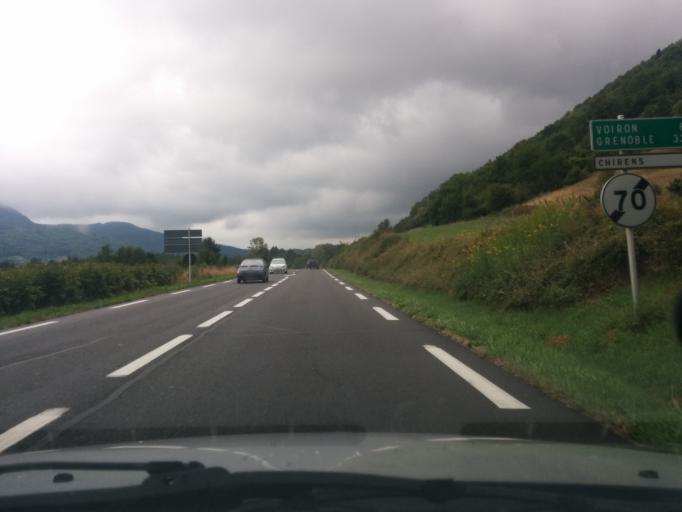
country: FR
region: Rhone-Alpes
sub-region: Departement de l'Isere
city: Chirens
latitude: 45.4271
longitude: 5.5623
